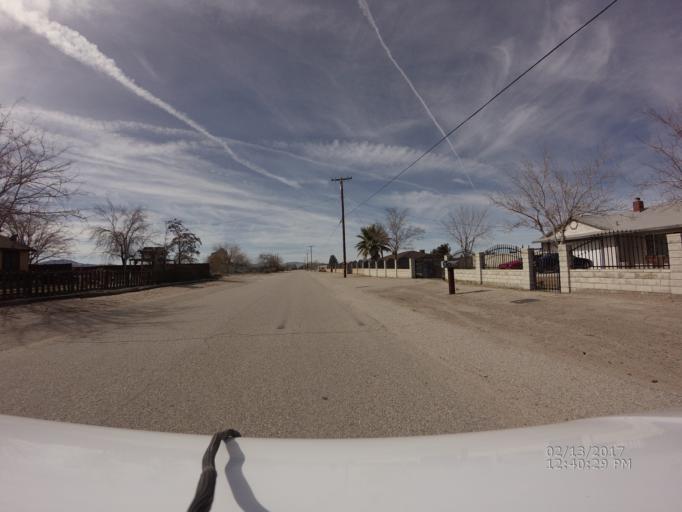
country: US
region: California
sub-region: Los Angeles County
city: Littlerock
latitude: 34.5708
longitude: -117.9278
